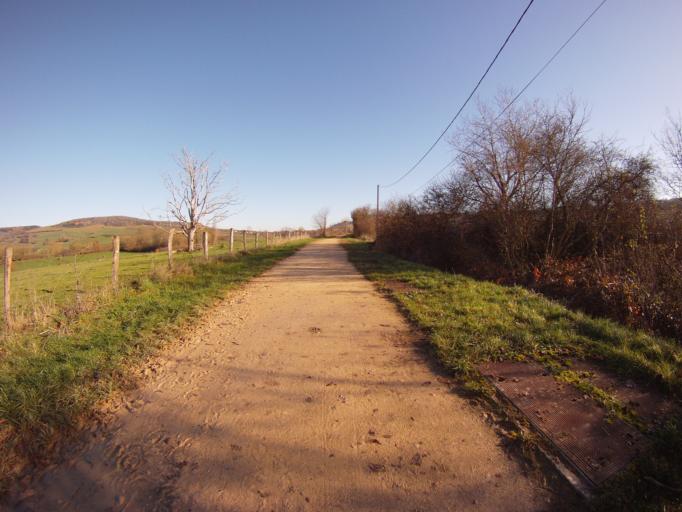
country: FR
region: Lorraine
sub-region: Departement de Meurthe-et-Moselle
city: Faulx
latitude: 48.7924
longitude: 6.2132
